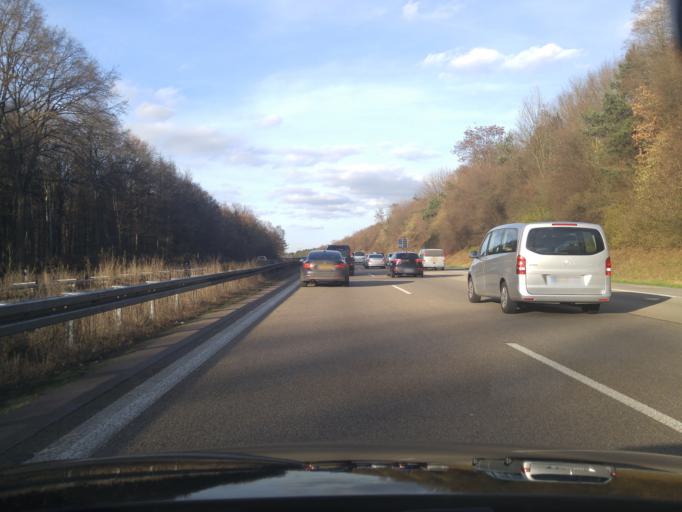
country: DE
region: North Rhine-Westphalia
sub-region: Regierungsbezirk Dusseldorf
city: Hilden
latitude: 51.1497
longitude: 6.9675
